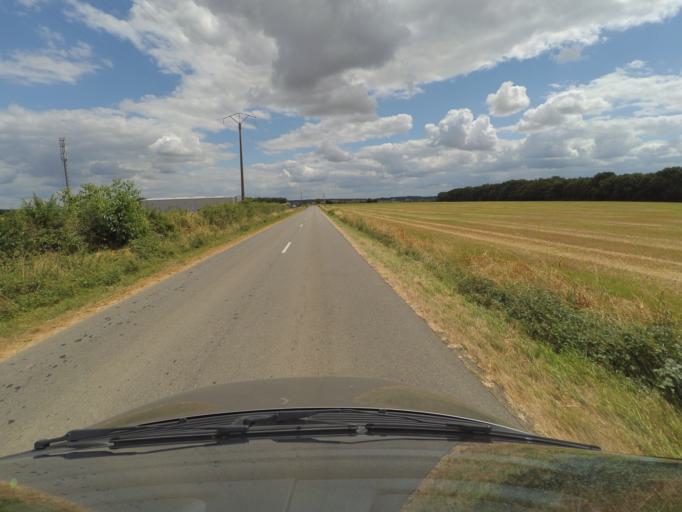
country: FR
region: Poitou-Charentes
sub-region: Departement de la Vienne
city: Saint-Savin
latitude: 46.5582
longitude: 0.9556
